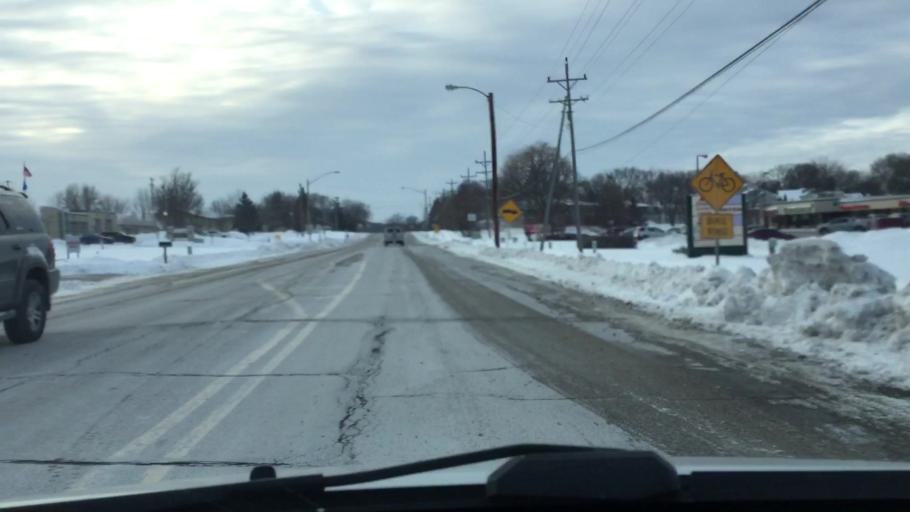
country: US
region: Wisconsin
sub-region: Waukesha County
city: Sussex
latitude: 43.1339
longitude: -88.2293
